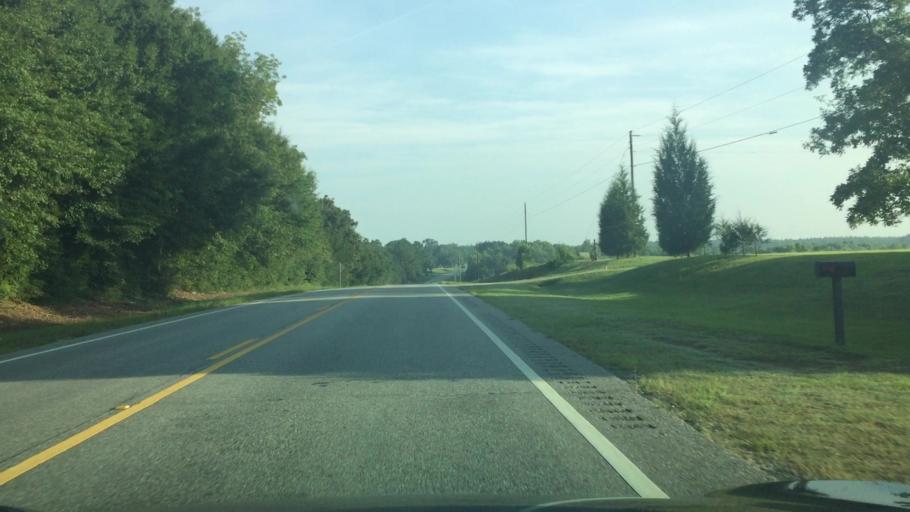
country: US
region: Alabama
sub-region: Covington County
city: Andalusia
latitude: 31.1331
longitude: -86.4581
